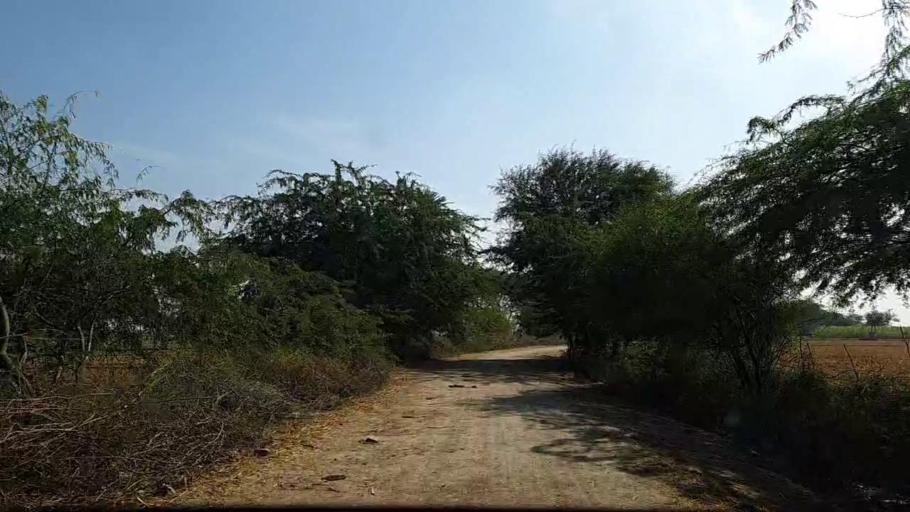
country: PK
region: Sindh
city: Daro Mehar
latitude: 24.7659
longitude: 68.1328
